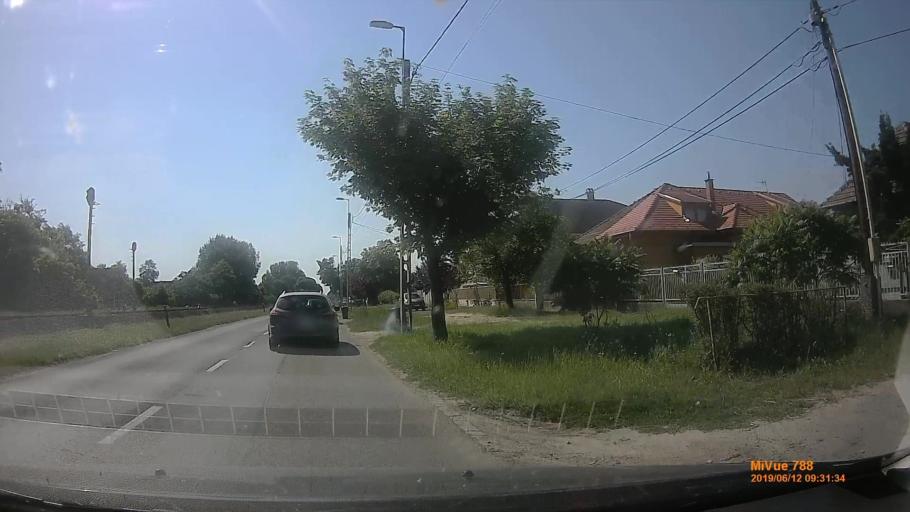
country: HU
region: Pest
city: Gyal
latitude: 47.4007
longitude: 19.1903
